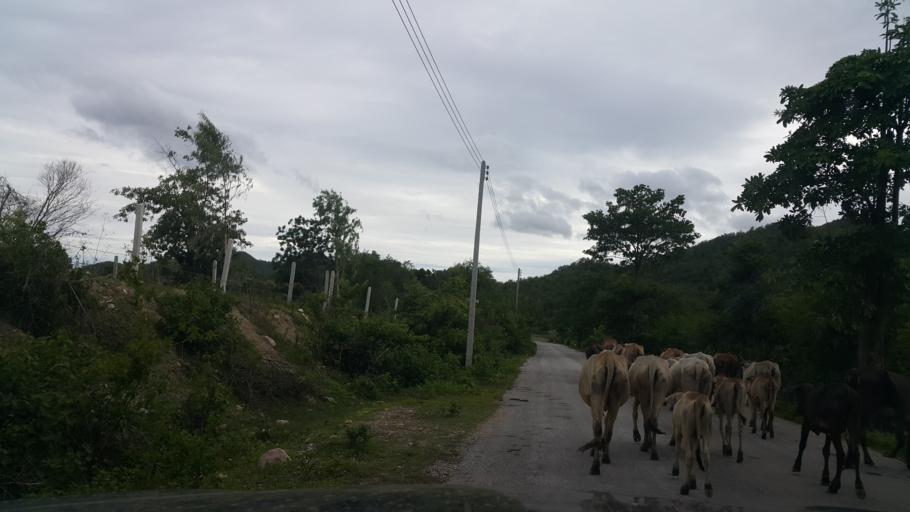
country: TH
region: Sukhothai
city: Thung Saliam
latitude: 17.1773
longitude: 99.4823
